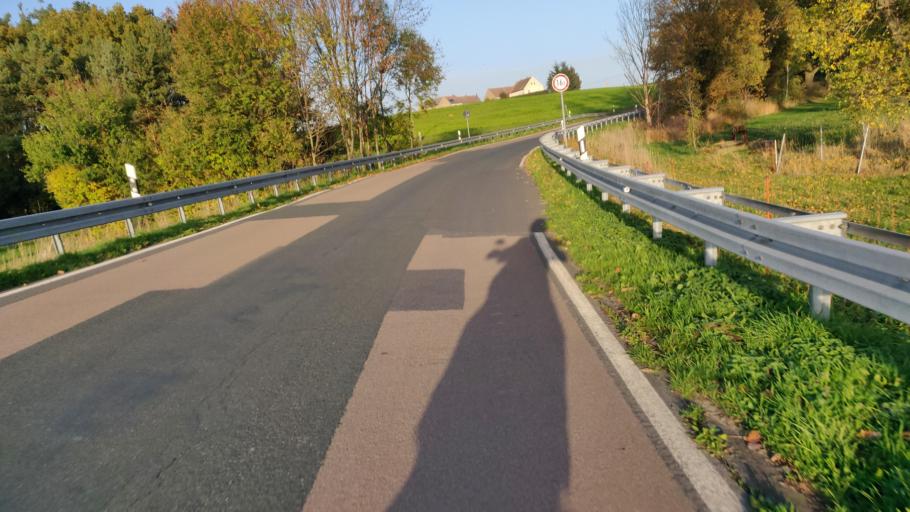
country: DE
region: Brandenburg
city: Hirschfeld
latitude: 51.3485
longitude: 13.6232
